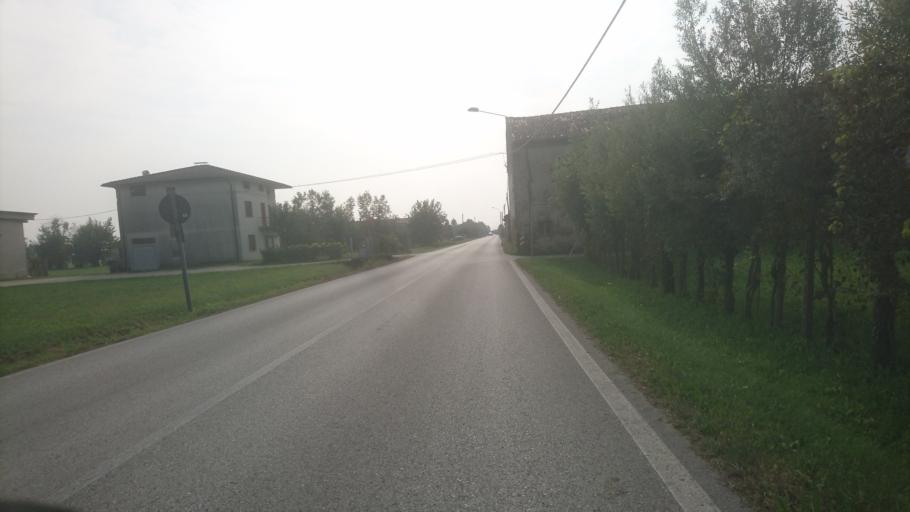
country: IT
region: Veneto
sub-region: Provincia di Vicenza
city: Quinto Vicentino
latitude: 45.5824
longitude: 11.6453
